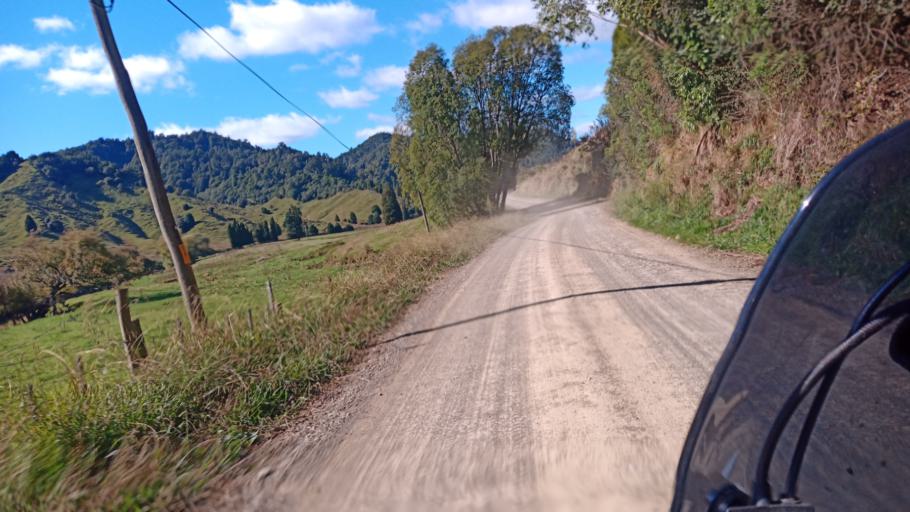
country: NZ
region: Bay of Plenty
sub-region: Opotiki District
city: Opotiki
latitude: -38.2538
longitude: 177.5793
